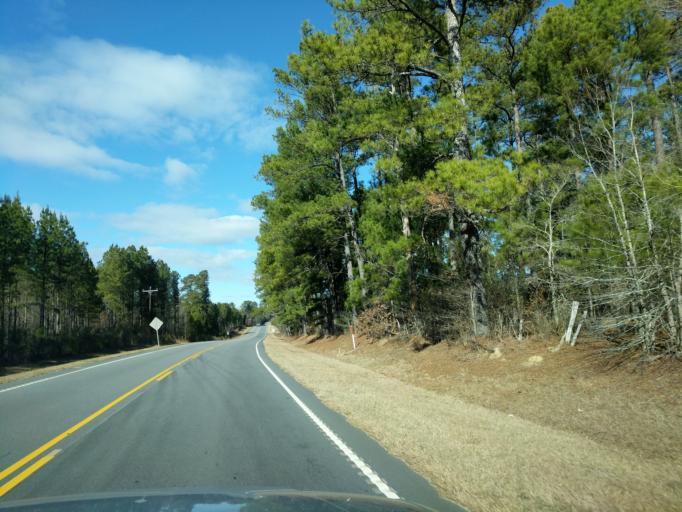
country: US
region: South Carolina
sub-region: Edgefield County
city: Edgefield
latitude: 33.9271
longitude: -82.0463
